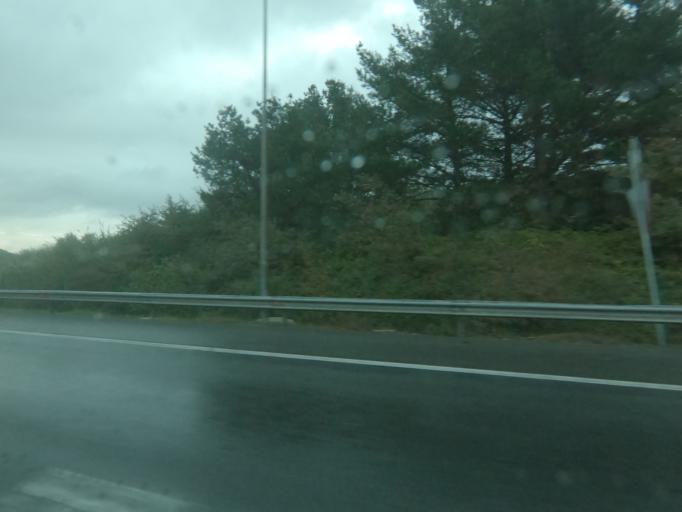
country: ES
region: Galicia
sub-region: Provincia de Pontevedra
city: Pontevedra
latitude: 42.4181
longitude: -8.6512
